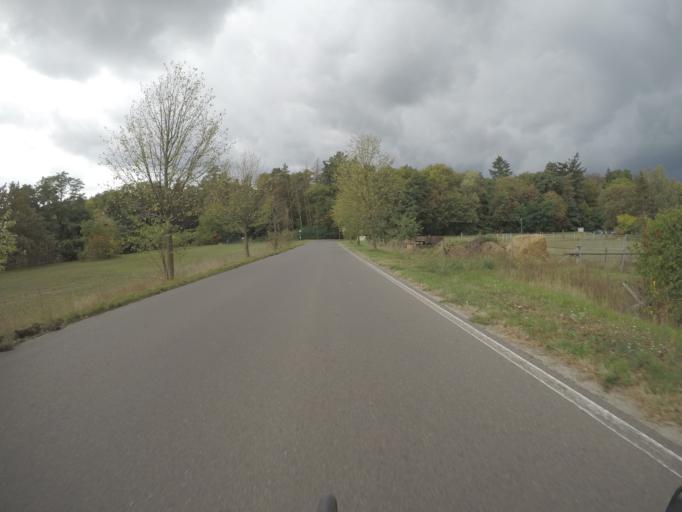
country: DE
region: Brandenburg
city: Strausberg
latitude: 52.6084
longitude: 13.9058
